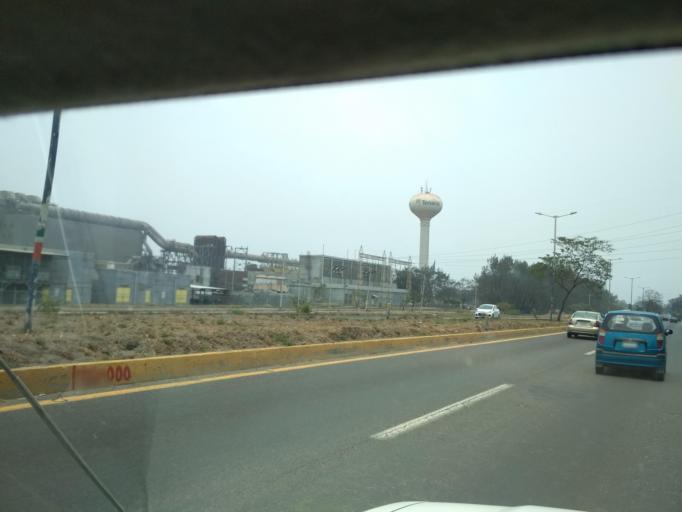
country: MX
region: Veracruz
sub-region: Veracruz
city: Oasis
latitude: 19.1768
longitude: -96.2434
